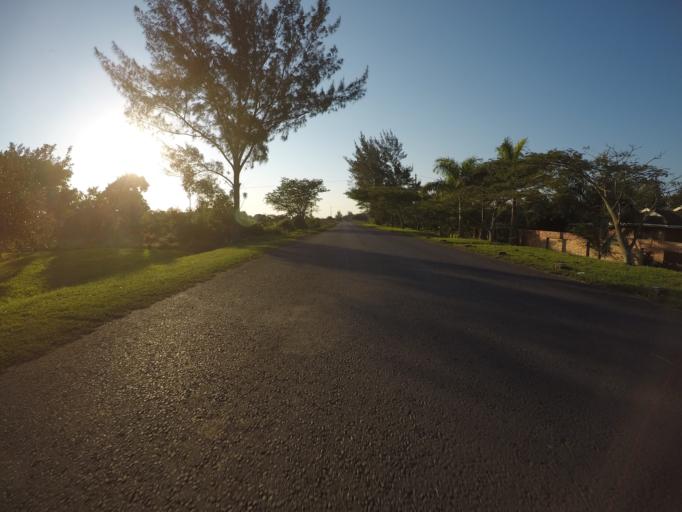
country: ZA
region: KwaZulu-Natal
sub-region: uThungulu District Municipality
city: KwaMbonambi
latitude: -28.6875
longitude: 32.2068
